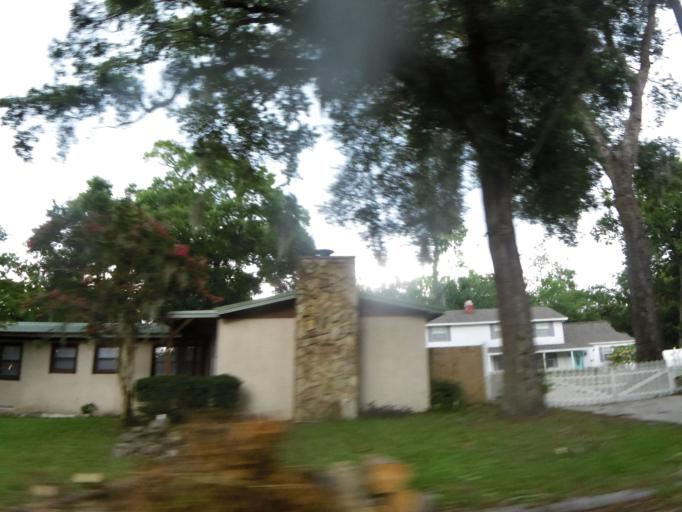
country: US
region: Florida
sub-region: Duval County
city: Jacksonville
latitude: 30.3444
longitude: -81.6052
